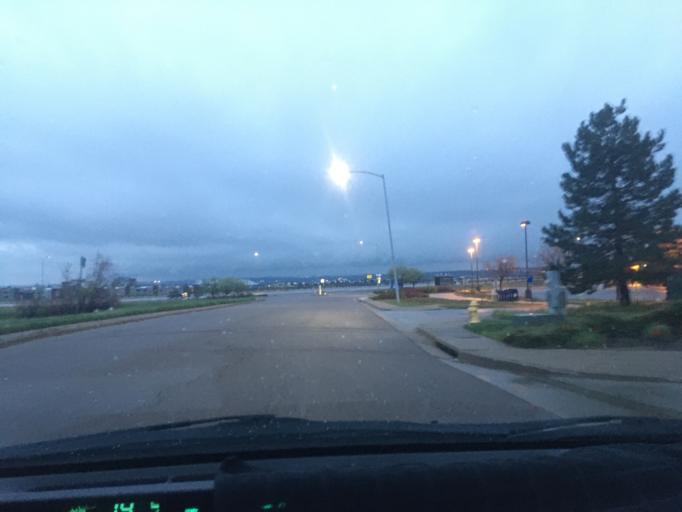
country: US
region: Colorado
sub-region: Broomfield County
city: Broomfield
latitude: 39.9034
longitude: -105.0981
